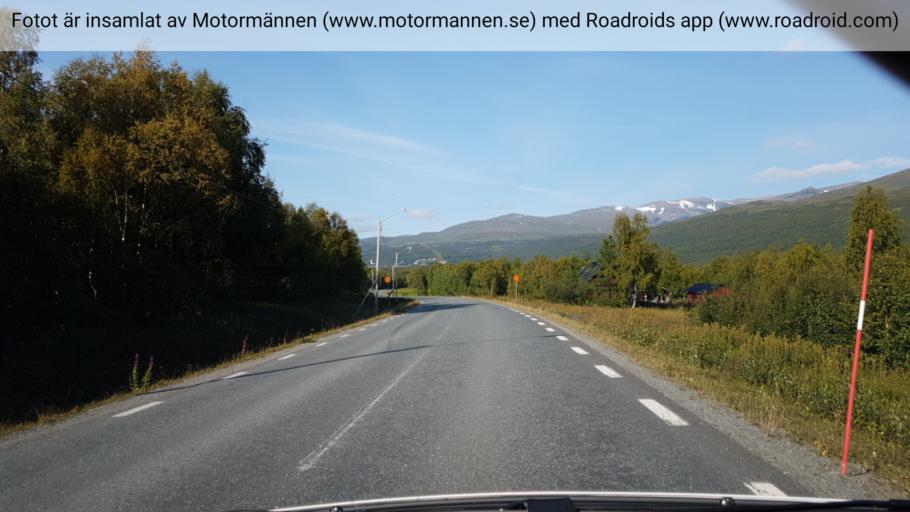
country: NO
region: Nordland
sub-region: Rana
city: Mo i Rana
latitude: 65.7738
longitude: 15.1127
